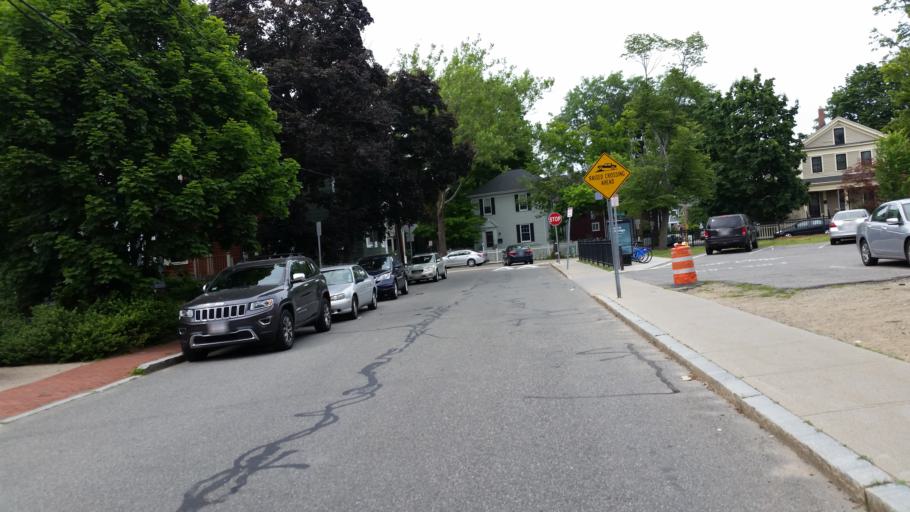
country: US
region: Massachusetts
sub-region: Middlesex County
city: Cambridge
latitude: 42.3924
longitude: -71.1291
